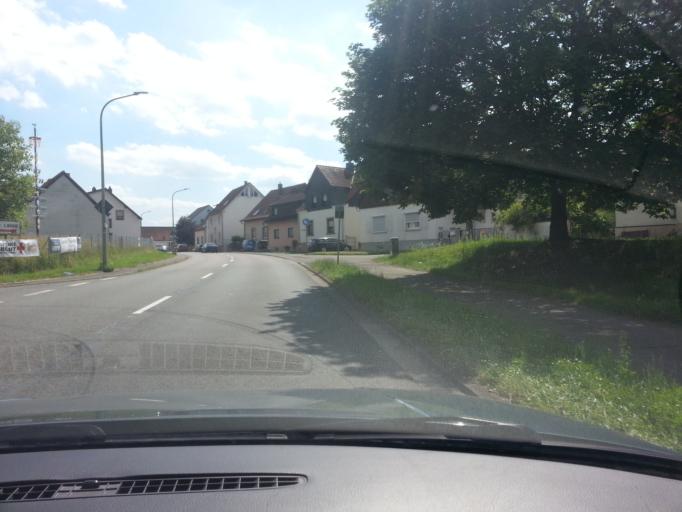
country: DE
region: Saarland
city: Blieskastel
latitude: 49.2326
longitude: 7.2683
